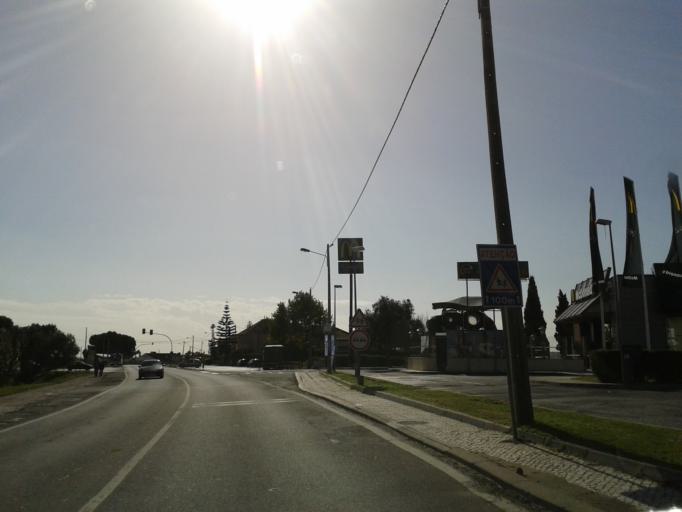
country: PT
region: Setubal
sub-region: Palmela
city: Palmela
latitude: 38.5674
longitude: -8.8880
